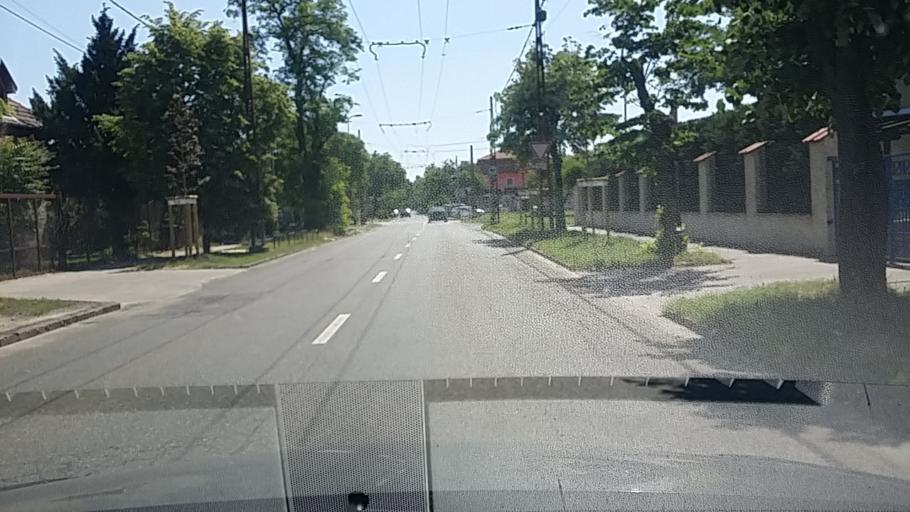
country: HU
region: Budapest
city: Budapest XIV. keruelet
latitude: 47.5249
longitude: 19.1320
